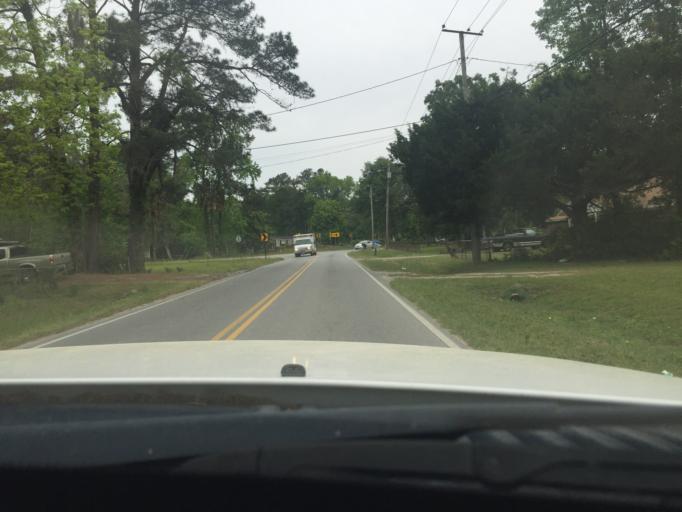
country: US
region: Georgia
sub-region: Chatham County
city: Georgetown
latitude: 31.9817
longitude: -81.2568
